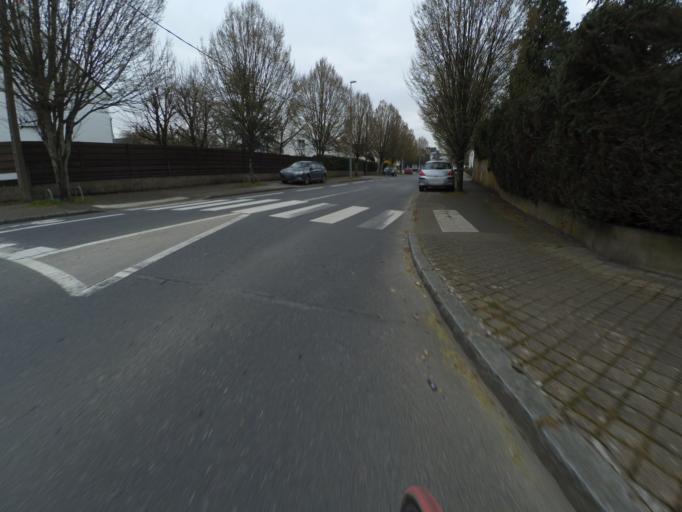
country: FR
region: Pays de la Loire
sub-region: Departement de la Loire-Atlantique
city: Carquefou
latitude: 47.2987
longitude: -1.4884
